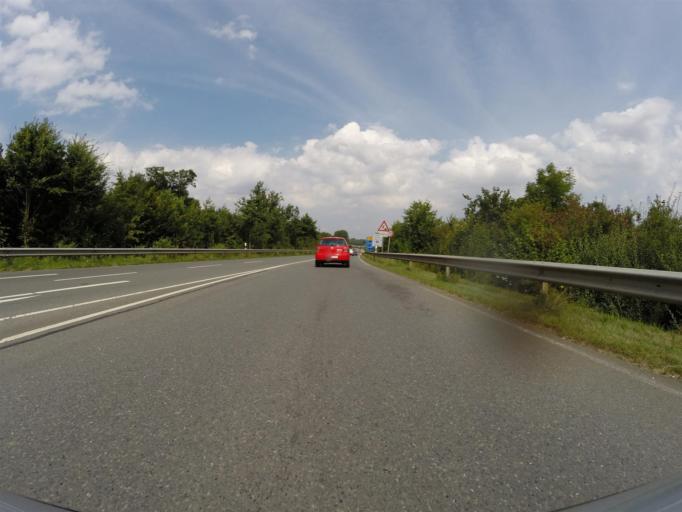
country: DE
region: North Rhine-Westphalia
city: Loehne
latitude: 52.1893
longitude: 8.6635
